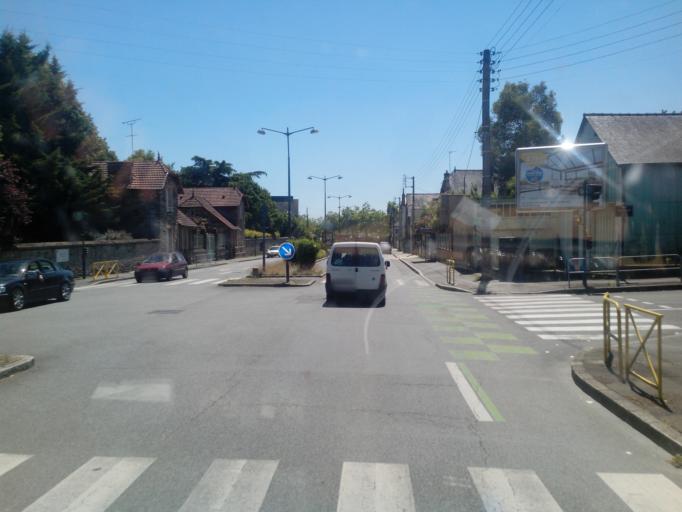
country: FR
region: Brittany
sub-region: Departement d'Ille-et-Vilaine
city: Rennes
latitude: 48.1159
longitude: -1.6485
